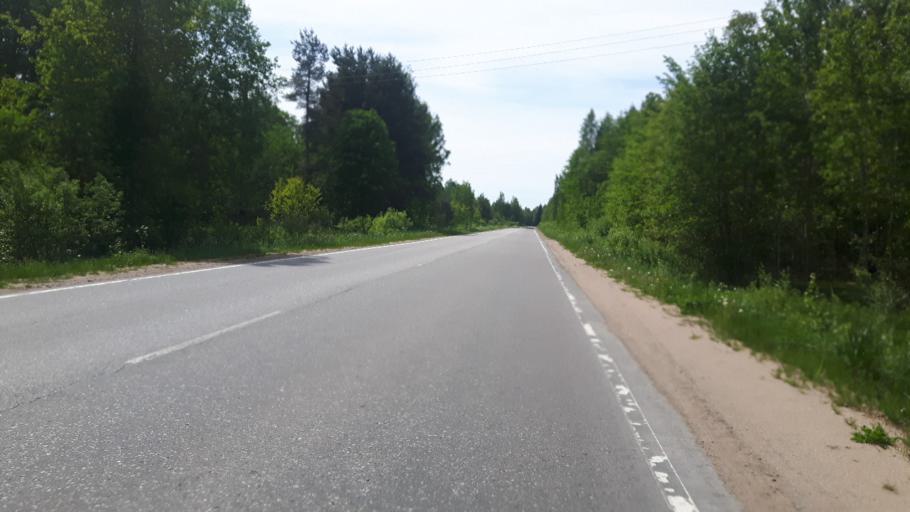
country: RU
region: Leningrad
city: Ust'-Luga
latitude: 59.6557
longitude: 28.2454
